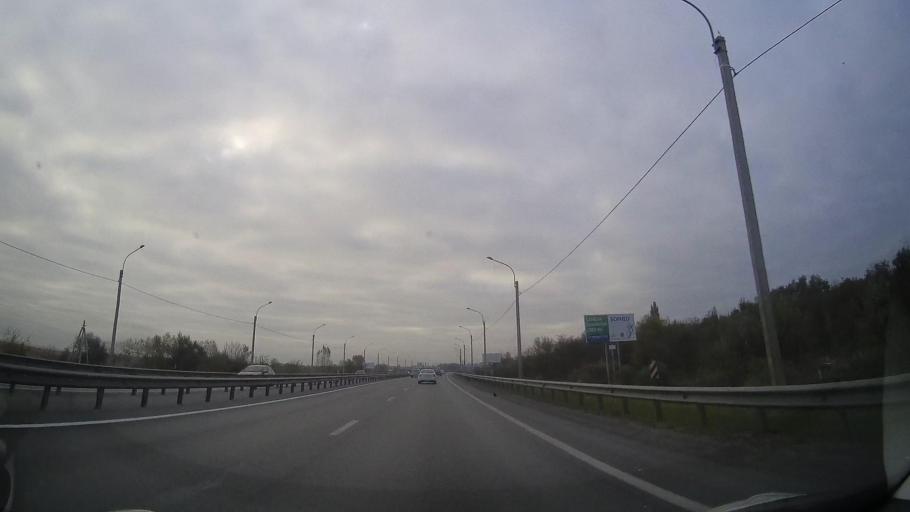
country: RU
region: Rostov
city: Bataysk
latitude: 47.1456
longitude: 39.7749
